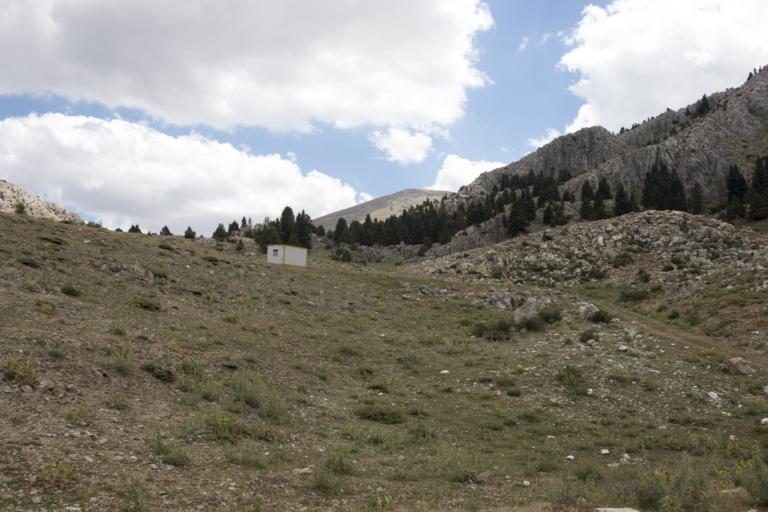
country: TR
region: Kayseri
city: Toklar
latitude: 38.3305
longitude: 36.0749
